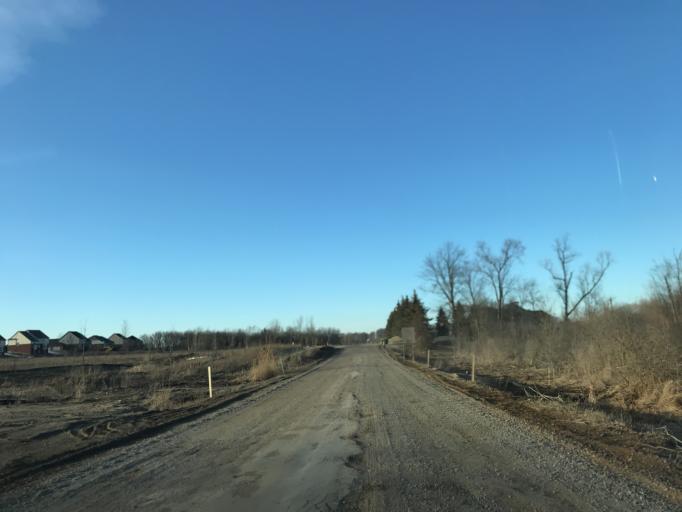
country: US
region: Michigan
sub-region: Oakland County
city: Wixom
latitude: 42.4596
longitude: -83.5533
